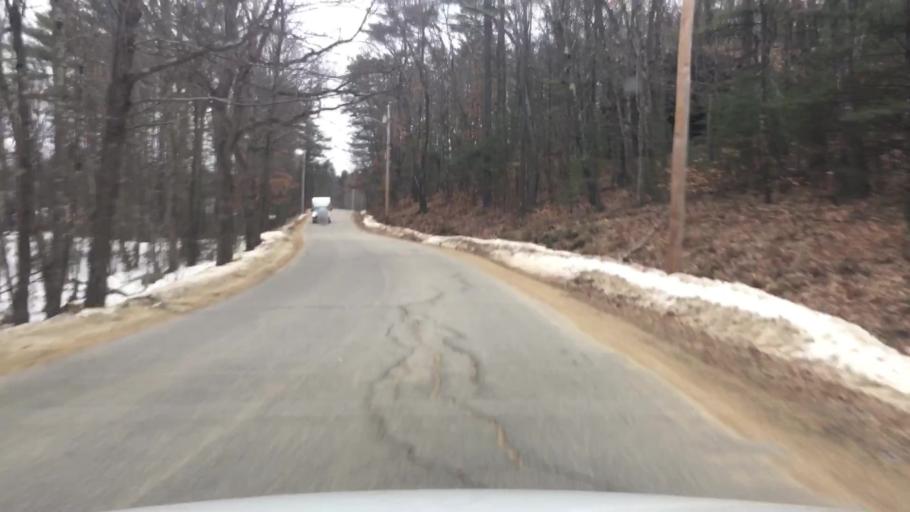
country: US
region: New Hampshire
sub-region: Strafford County
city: Rochester
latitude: 43.3422
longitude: -70.9556
